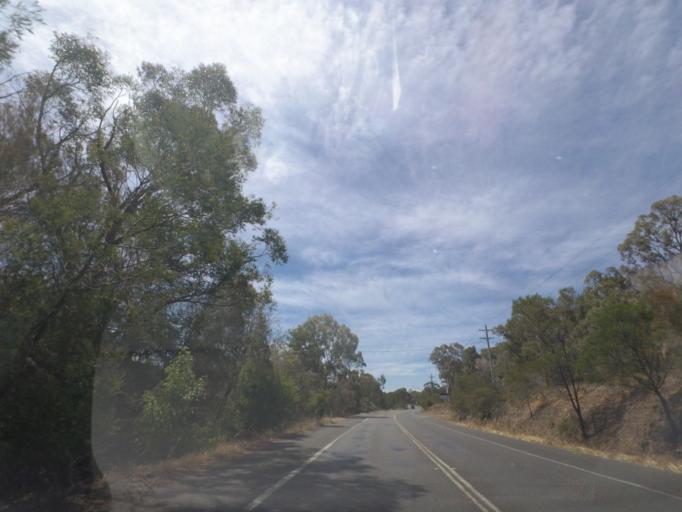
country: AU
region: New South Wales
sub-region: Wollondilly
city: Buxton
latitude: -34.2639
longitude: 150.5730
